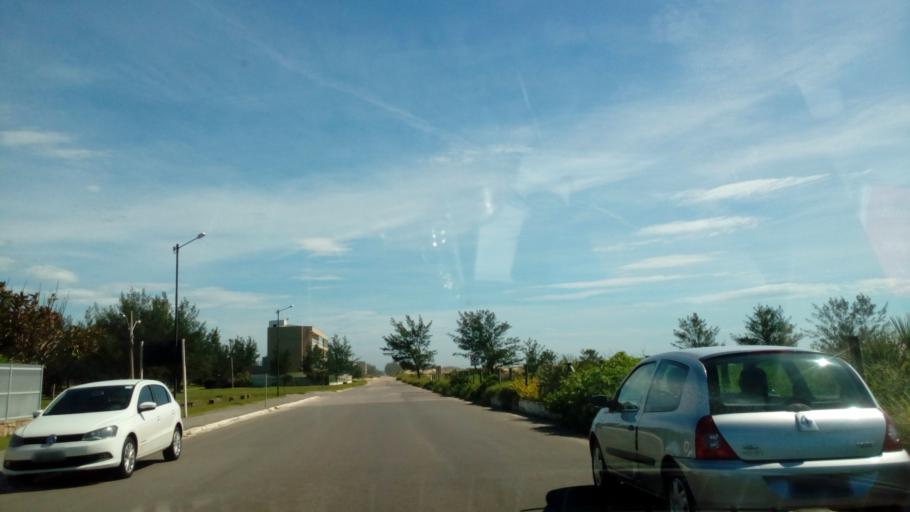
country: BR
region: Santa Catarina
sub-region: Laguna
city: Laguna
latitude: -28.4641
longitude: -48.7673
